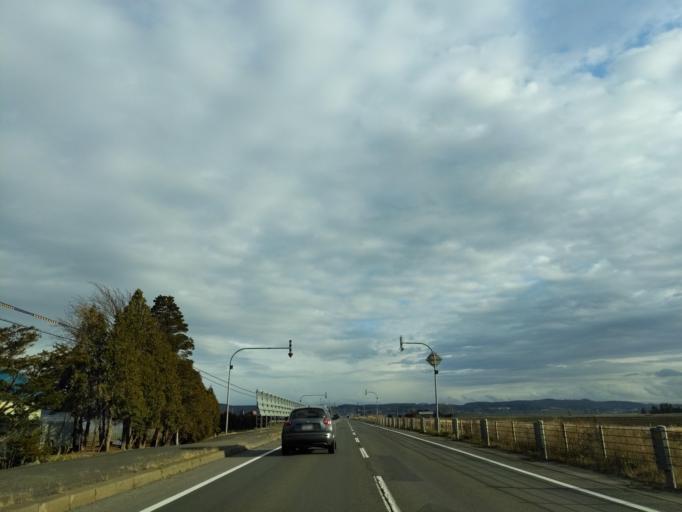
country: JP
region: Hokkaido
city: Kitahiroshima
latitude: 42.9602
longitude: 141.6901
